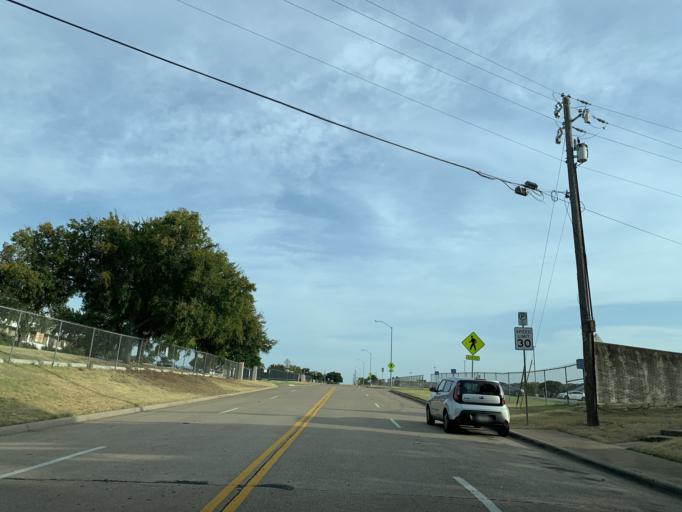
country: US
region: Texas
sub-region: Dallas County
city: Cockrell Hill
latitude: 32.6974
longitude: -96.8988
